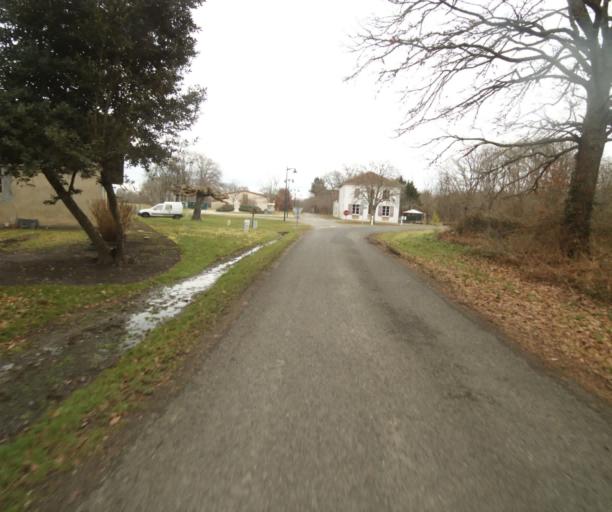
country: FR
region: Aquitaine
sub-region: Departement des Landes
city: Gabarret
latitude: 44.0099
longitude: -0.0230
